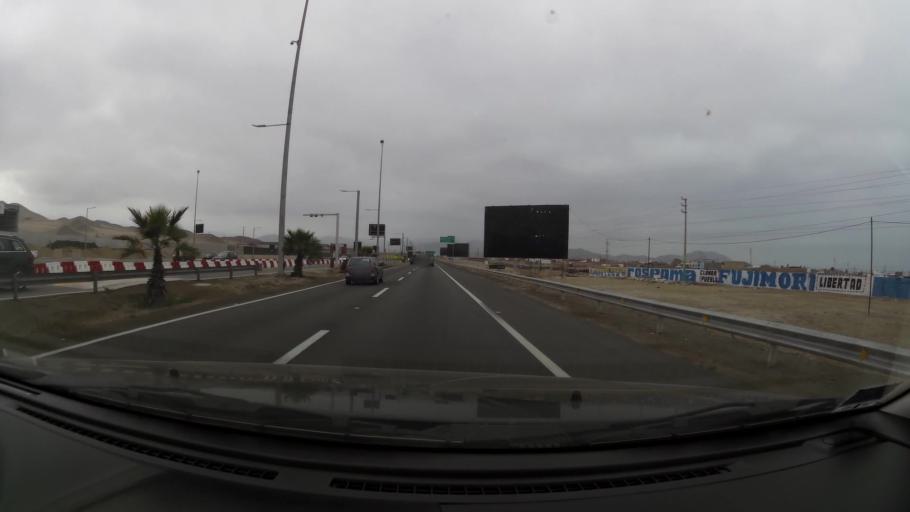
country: PE
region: Lima
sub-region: Lima
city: San Bartolo
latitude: -12.3672
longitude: -76.7891
